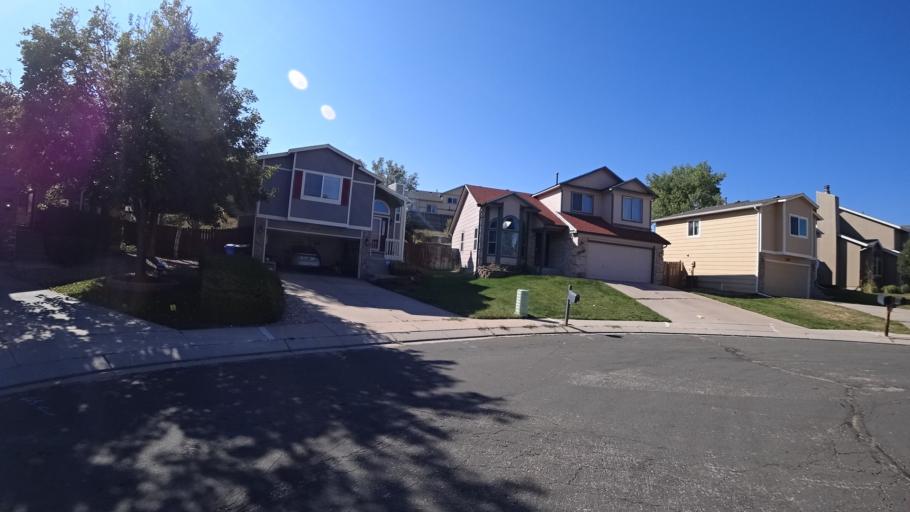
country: US
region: Colorado
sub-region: El Paso County
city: Cimarron Hills
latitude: 38.8720
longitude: -104.7065
